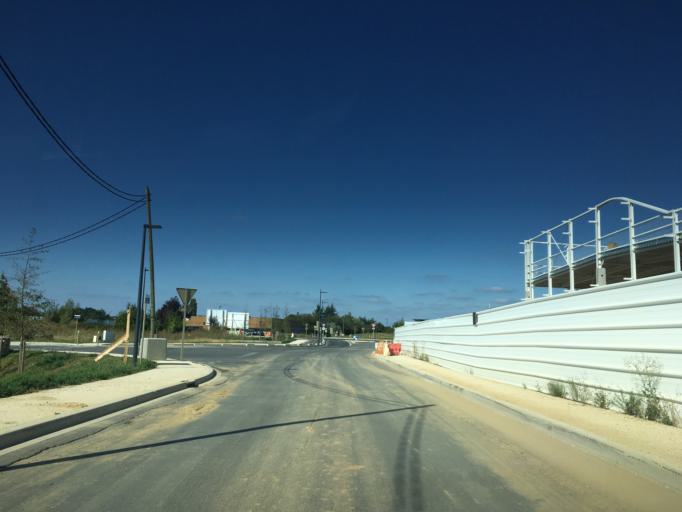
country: FR
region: Ile-de-France
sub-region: Departement de Seine-et-Marne
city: Servon
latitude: 48.7079
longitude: 2.5846
